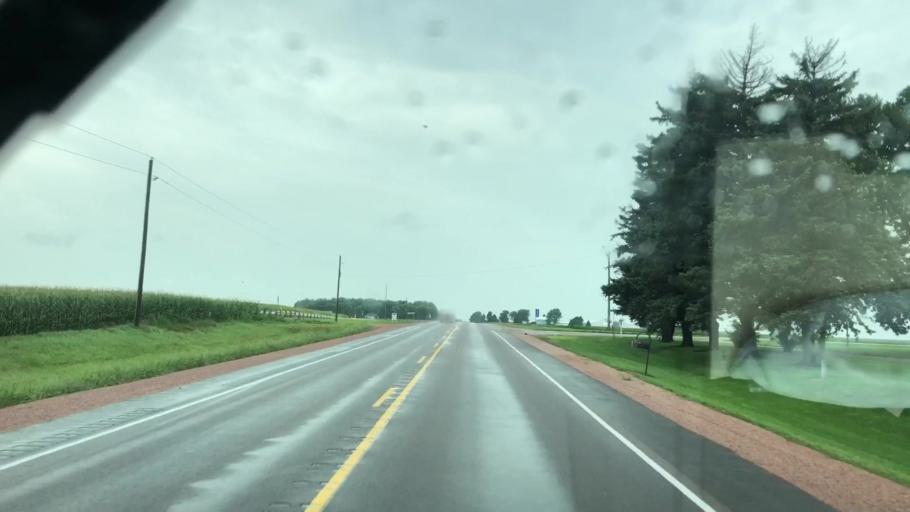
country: US
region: Iowa
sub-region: O'Brien County
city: Sheldon
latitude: 43.1862
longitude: -95.7812
